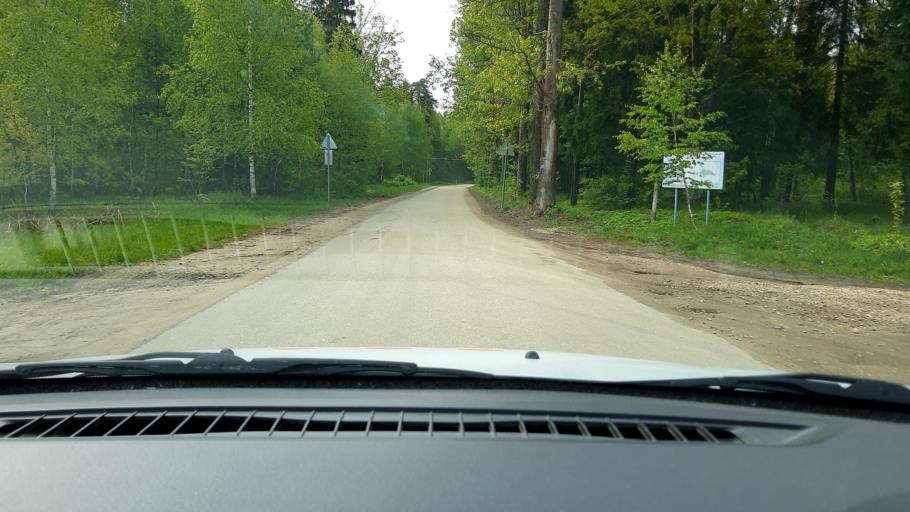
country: RU
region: Nizjnij Novgorod
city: Afonino
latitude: 56.1880
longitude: 44.0777
